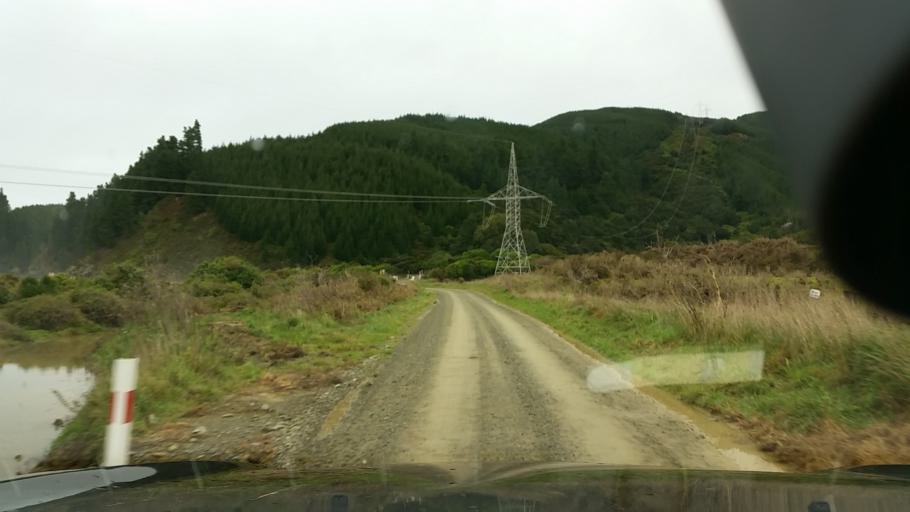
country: NZ
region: Marlborough
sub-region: Marlborough District
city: Picton
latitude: -41.3566
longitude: 174.0705
